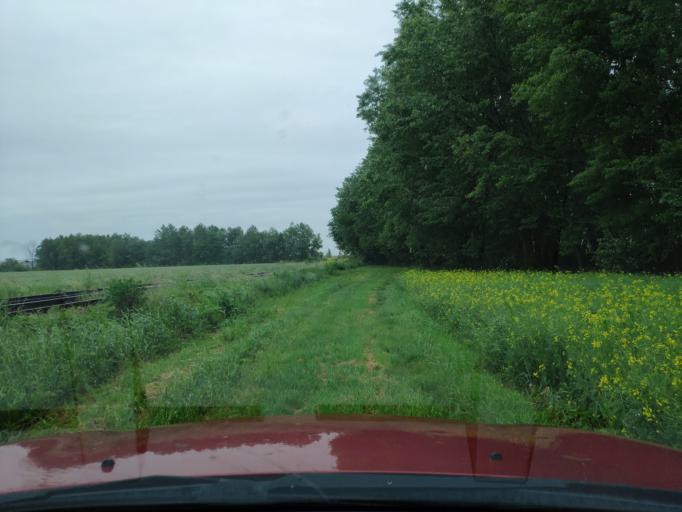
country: SK
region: Kosicky
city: Cierna nad Tisou
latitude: 48.4172
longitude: 22.0421
